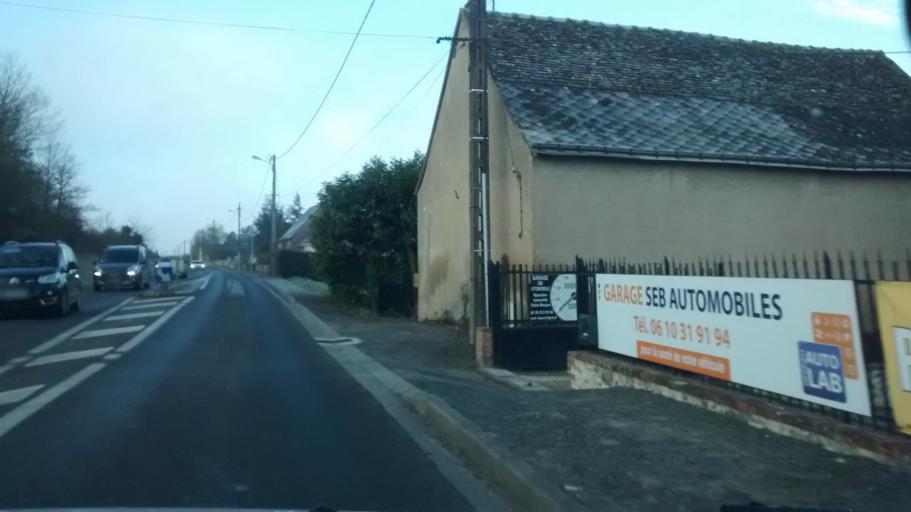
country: FR
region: Centre
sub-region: Departement d'Indre-et-Loire
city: Ballan-Mire
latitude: 47.3588
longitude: 0.6043
